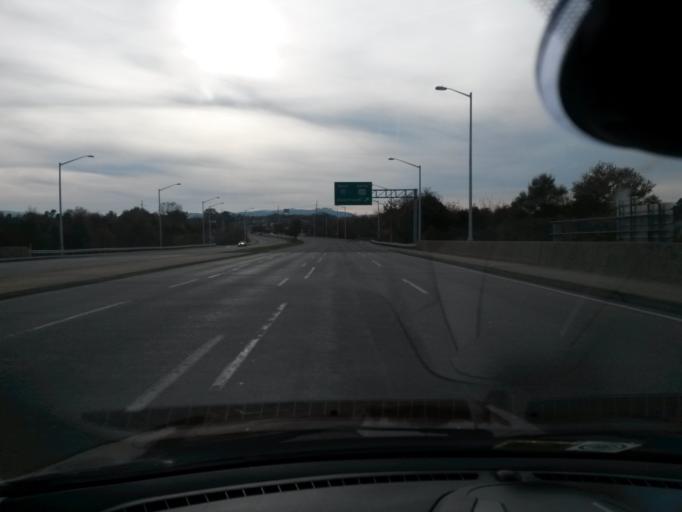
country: US
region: Virginia
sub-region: Roanoke County
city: Hollins
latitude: 37.3090
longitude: -79.9737
